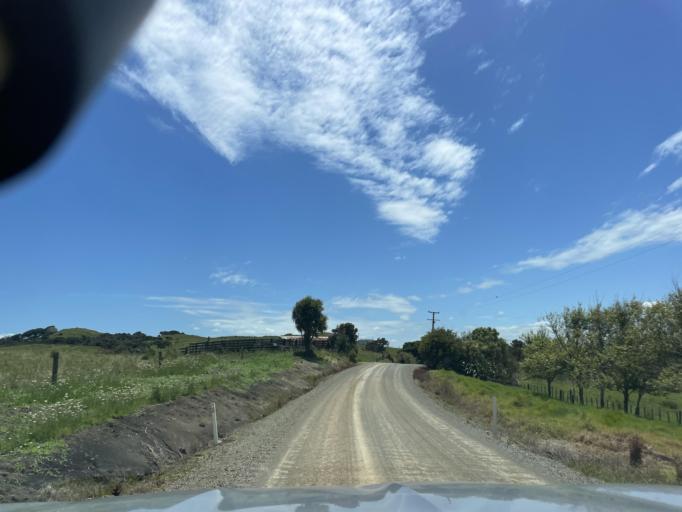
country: NZ
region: Auckland
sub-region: Auckland
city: Wellsford
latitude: -36.2226
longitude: 174.3624
